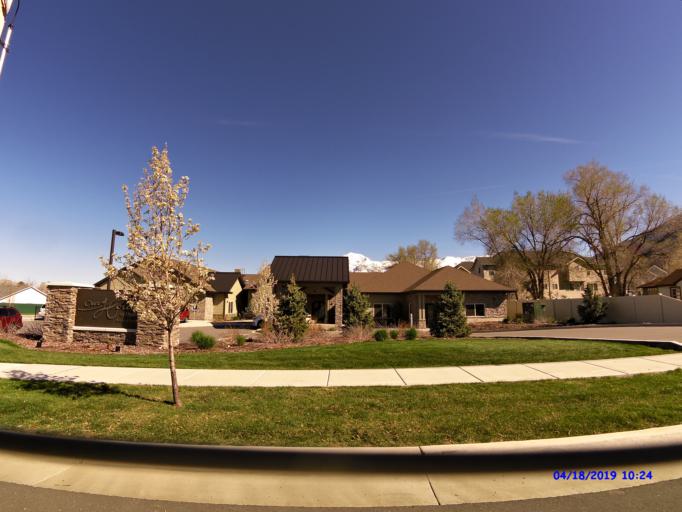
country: US
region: Utah
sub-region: Weber County
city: Harrisville
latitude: 41.2666
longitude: -111.9640
